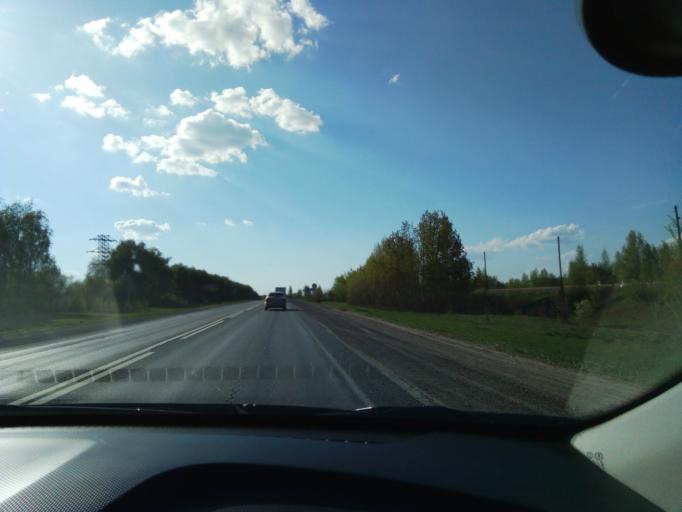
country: RU
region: Chuvashia
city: Kugesi
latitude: 56.0554
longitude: 47.2707
